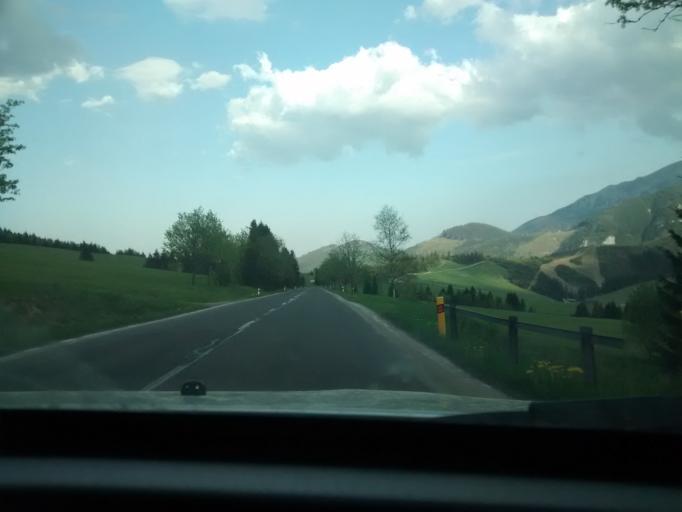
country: SK
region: Presovsky
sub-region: Okres Poprad
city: Zdiar
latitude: 49.2790
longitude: 20.2148
